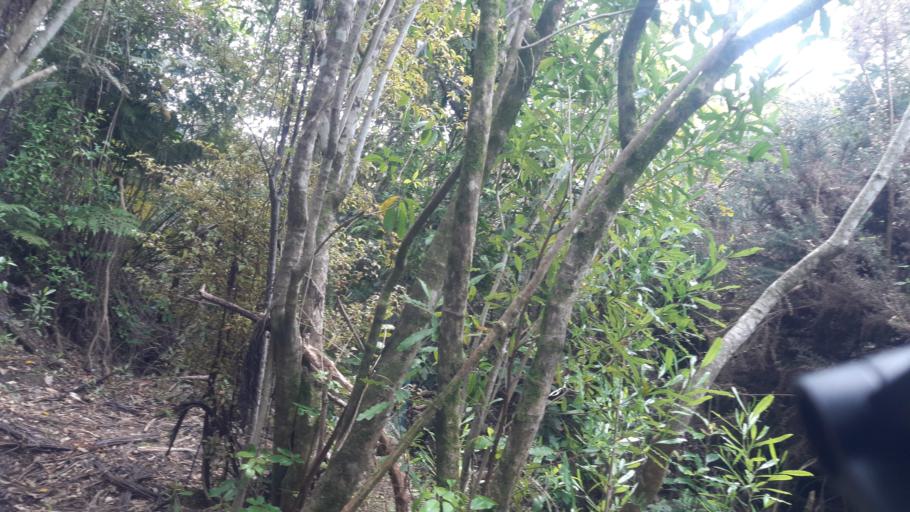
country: NZ
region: Marlborough
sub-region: Marlborough District
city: Picton
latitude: -41.2635
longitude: 174.0014
